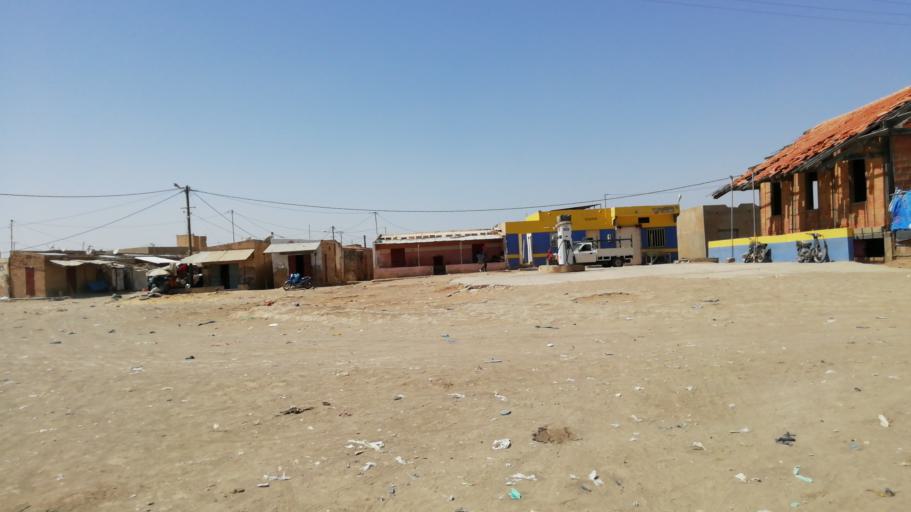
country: SN
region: Saint-Louis
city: Rosso
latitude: 16.4008
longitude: -16.0753
